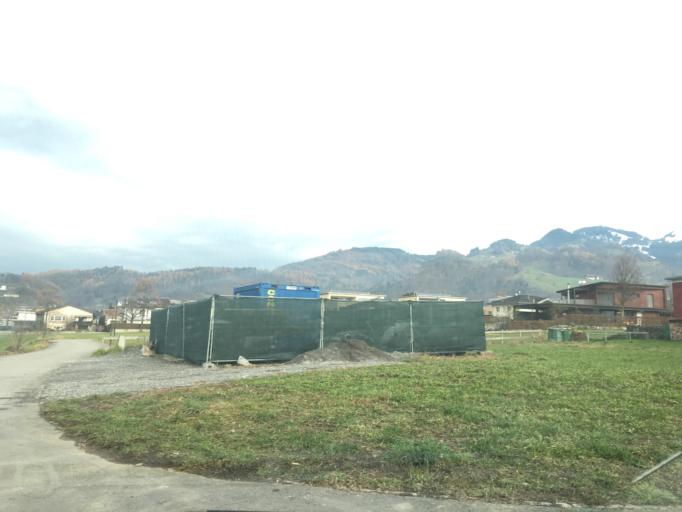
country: AT
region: Vorarlberg
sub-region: Politischer Bezirk Feldkirch
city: Weiler
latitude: 47.3003
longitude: 9.6441
